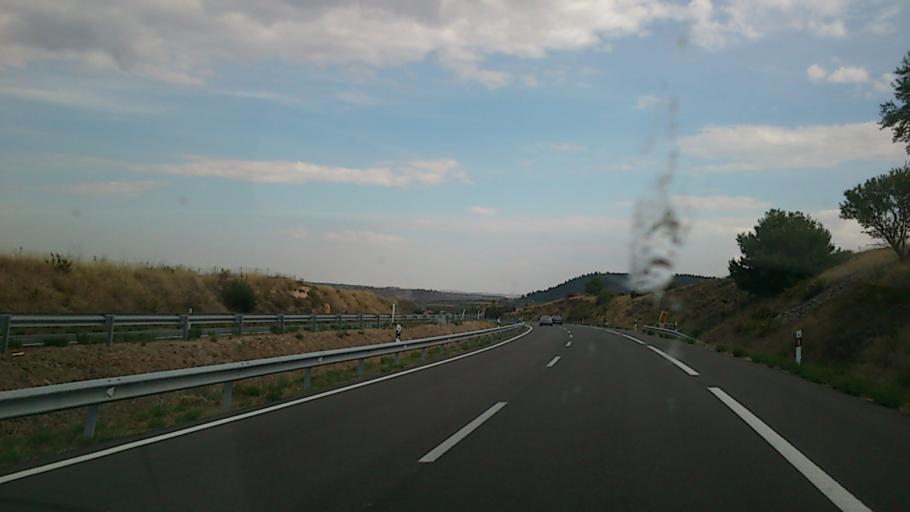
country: ES
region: La Rioja
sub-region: Provincia de La Rioja
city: Briones
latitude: 42.5380
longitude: -2.8039
